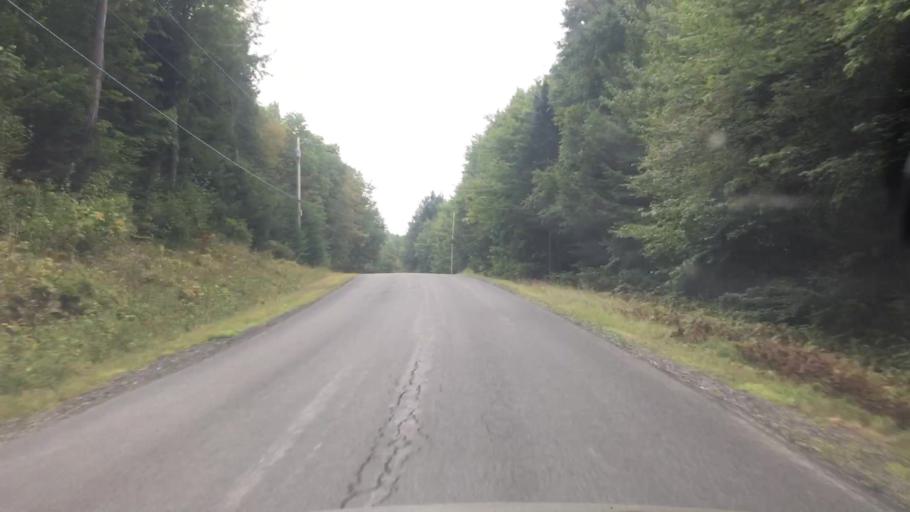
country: US
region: Vermont
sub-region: Windham County
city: Dover
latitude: 42.8420
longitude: -72.8283
